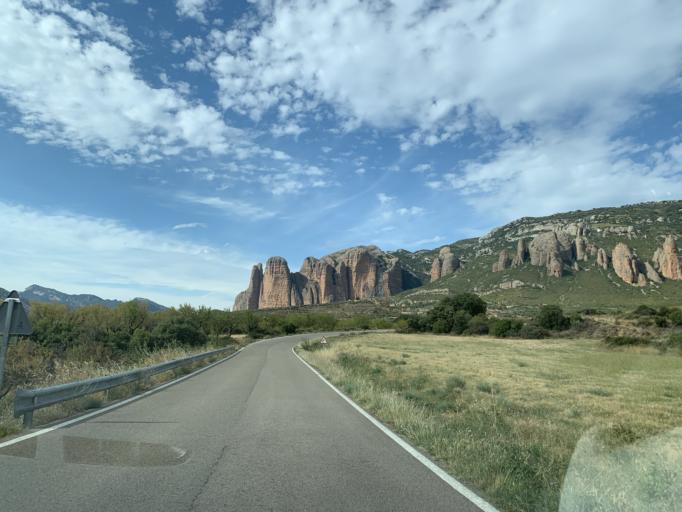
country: ES
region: Aragon
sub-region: Provincia de Zaragoza
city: Santa Eulalia de Gallego
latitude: 42.3321
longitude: -0.7231
